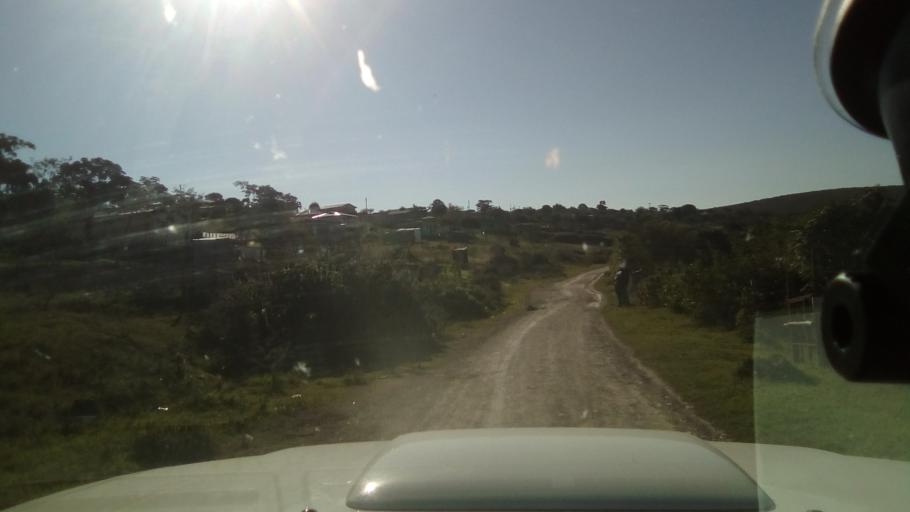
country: ZA
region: Eastern Cape
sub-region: Buffalo City Metropolitan Municipality
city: Bhisho
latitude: -32.8033
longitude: 27.3409
